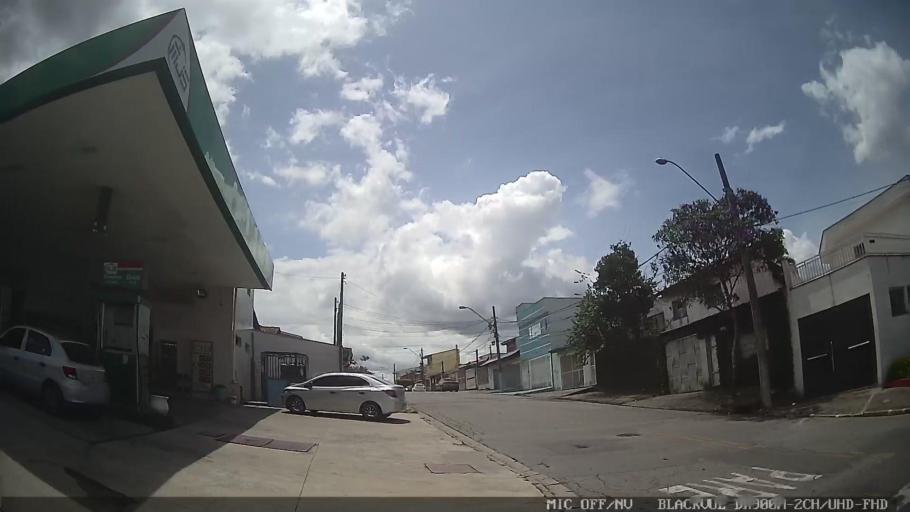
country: BR
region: Sao Paulo
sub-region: Mogi das Cruzes
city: Mogi das Cruzes
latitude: -23.5513
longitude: -46.2060
